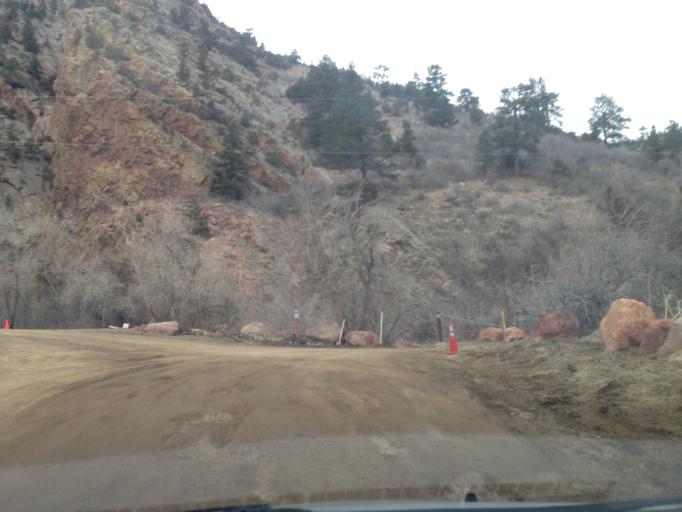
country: US
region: Colorado
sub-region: Boulder County
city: Boulder
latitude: 39.9323
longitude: -105.2798
